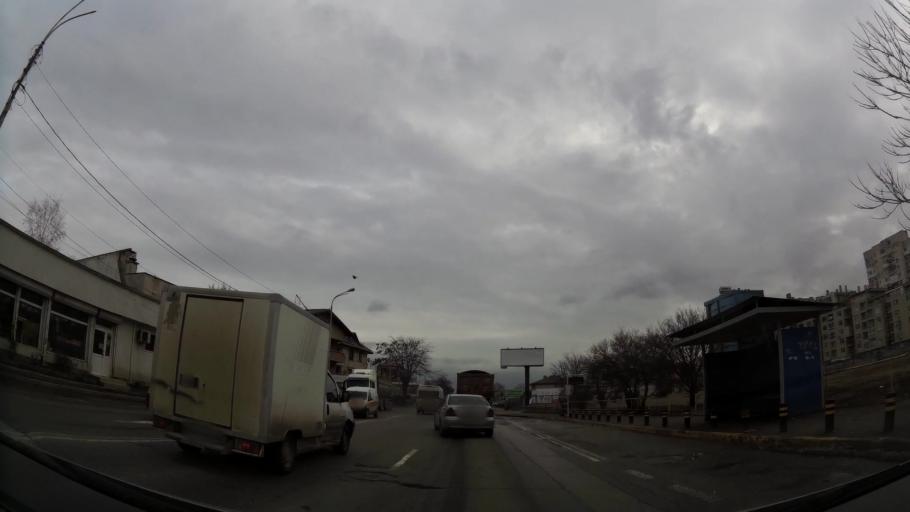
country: BG
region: Sofiya
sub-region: Obshtina Bozhurishte
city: Bozhurishte
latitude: 42.7318
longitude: 23.2532
